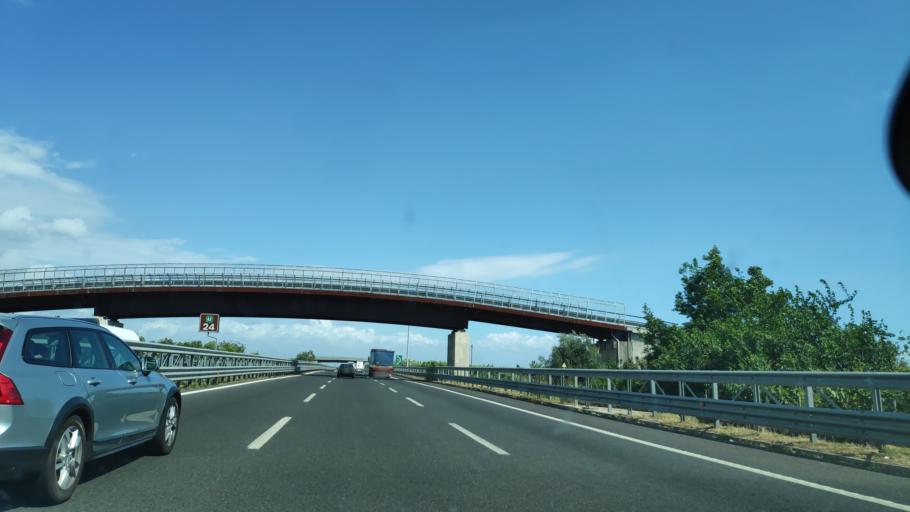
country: IT
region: Campania
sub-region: Provincia di Salerno
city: Pontecagnano
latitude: 40.6485
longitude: 14.8825
